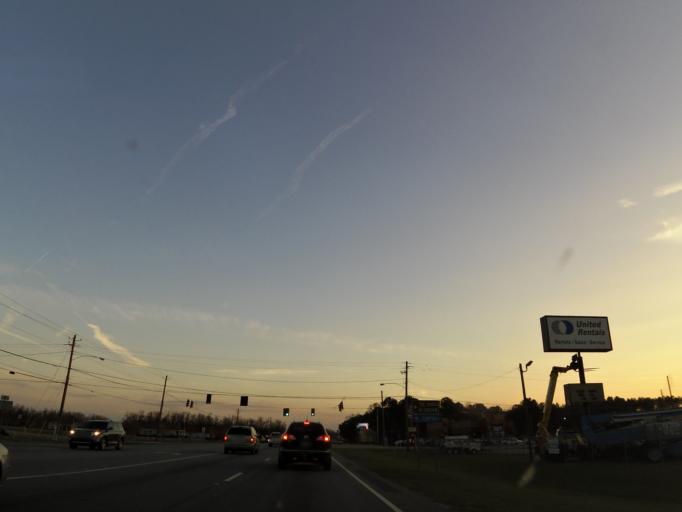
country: US
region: Georgia
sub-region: Lee County
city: Leesburg
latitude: 31.6575
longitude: -84.1730
